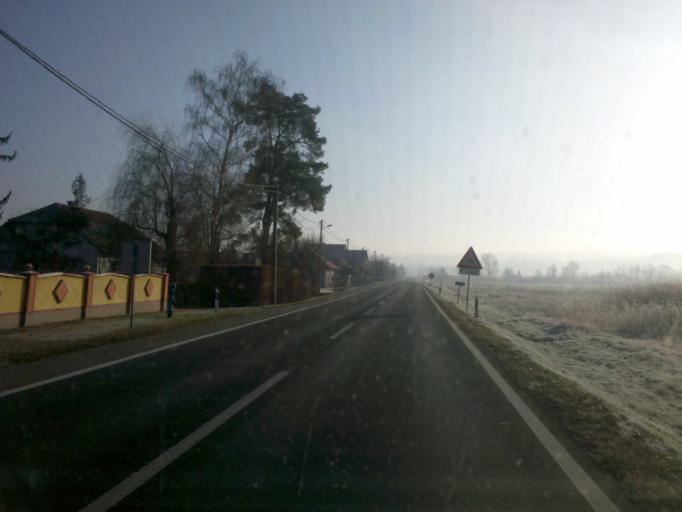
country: HR
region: Koprivnicko-Krizevacka
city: Reka
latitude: 46.1985
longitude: 16.7186
